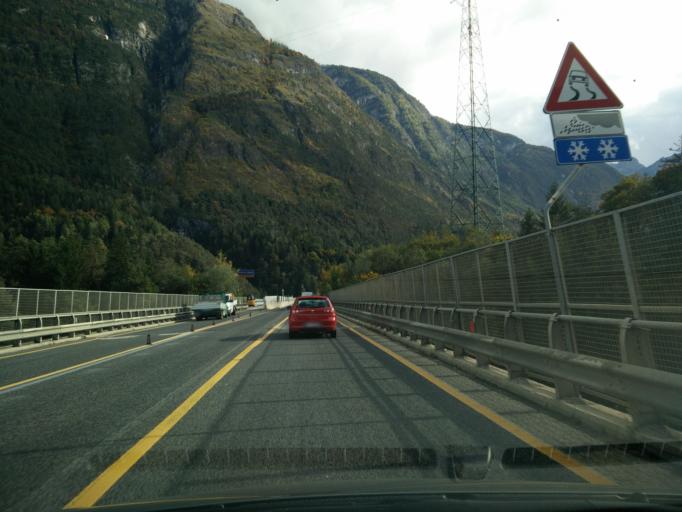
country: IT
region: Veneto
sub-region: Provincia di Belluno
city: Perarolo di Cadore
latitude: 46.4051
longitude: 12.3701
